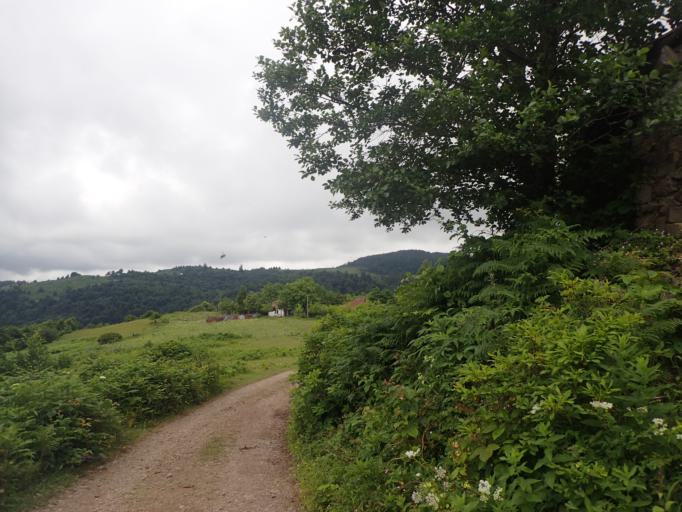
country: TR
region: Ordu
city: Akkus
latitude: 40.8604
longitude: 37.0185
